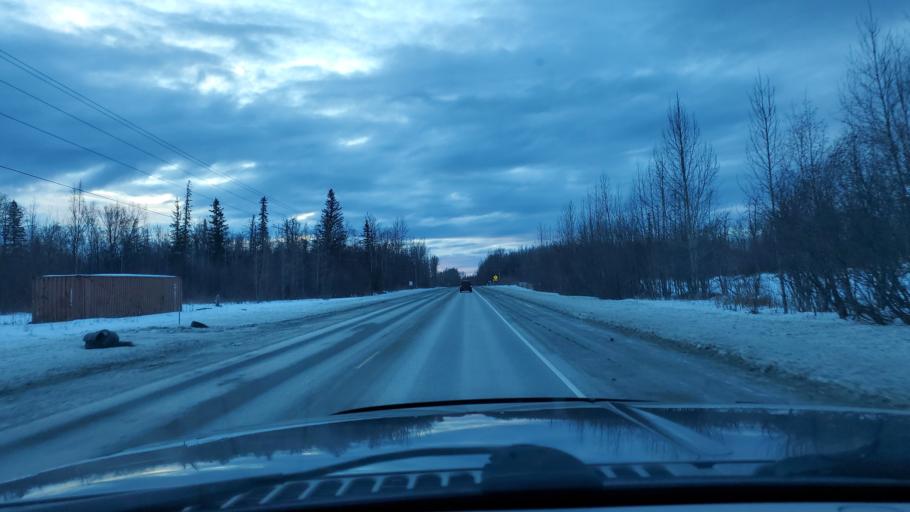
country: US
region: Alaska
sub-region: Matanuska-Susitna Borough
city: Farm Loop
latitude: 61.6661
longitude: -149.0826
